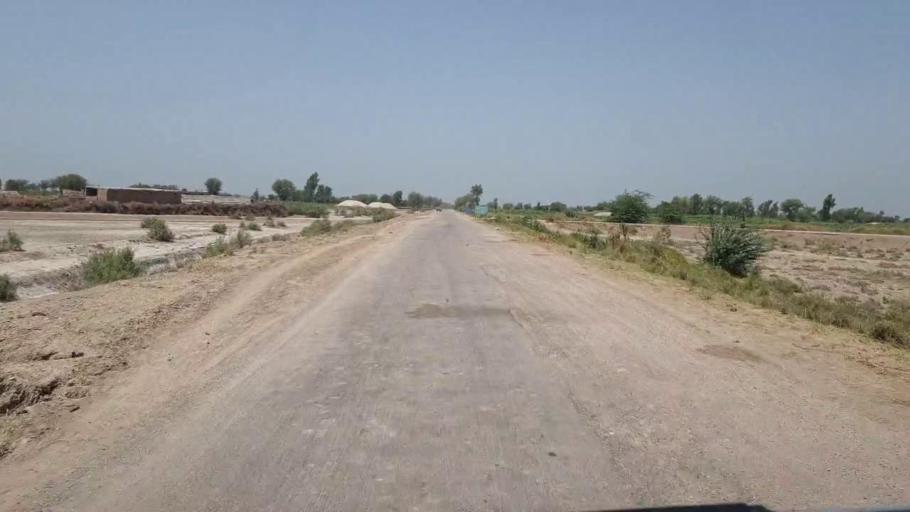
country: PK
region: Sindh
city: Nawabshah
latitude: 26.3569
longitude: 68.4006
